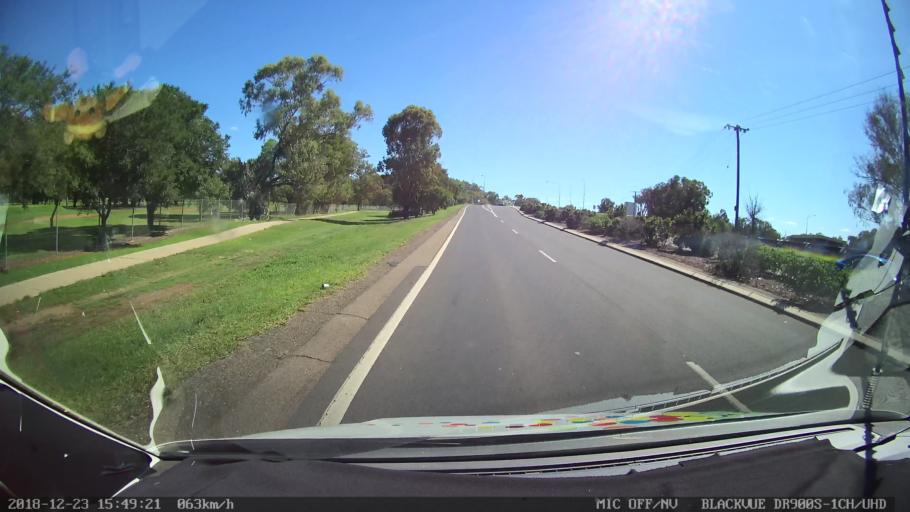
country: AU
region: New South Wales
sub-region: Tamworth Municipality
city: South Tamworth
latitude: -31.0986
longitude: 150.9073
